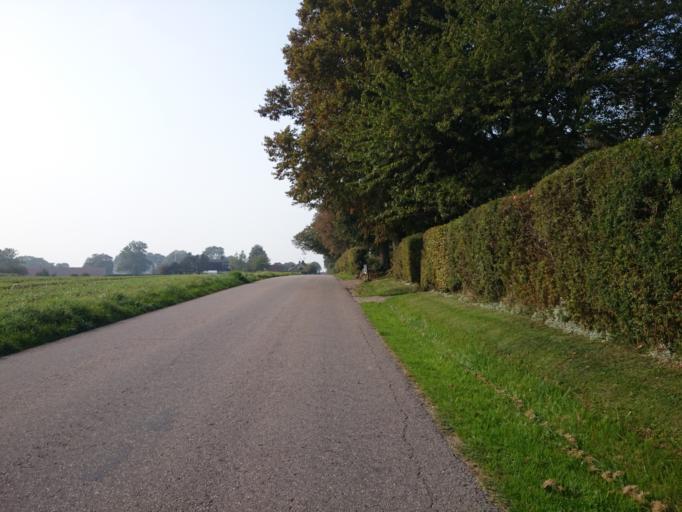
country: SE
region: Skane
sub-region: Helsingborg
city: Rydeback
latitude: 55.9058
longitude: 12.7037
